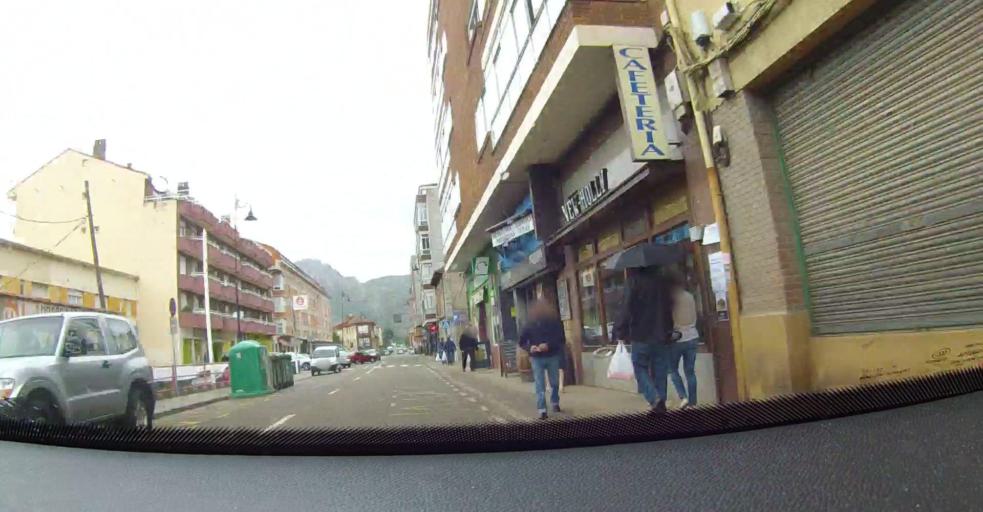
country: ES
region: Castille and Leon
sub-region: Provincia de Leon
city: Cistierna
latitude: 42.8046
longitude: -5.1289
